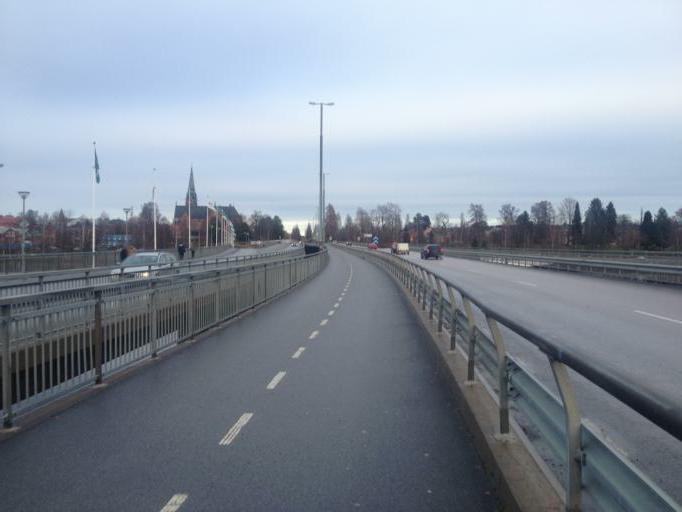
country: SE
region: Vaesterbotten
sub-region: Umea Kommun
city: Umea
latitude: 63.8199
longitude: 20.2662
